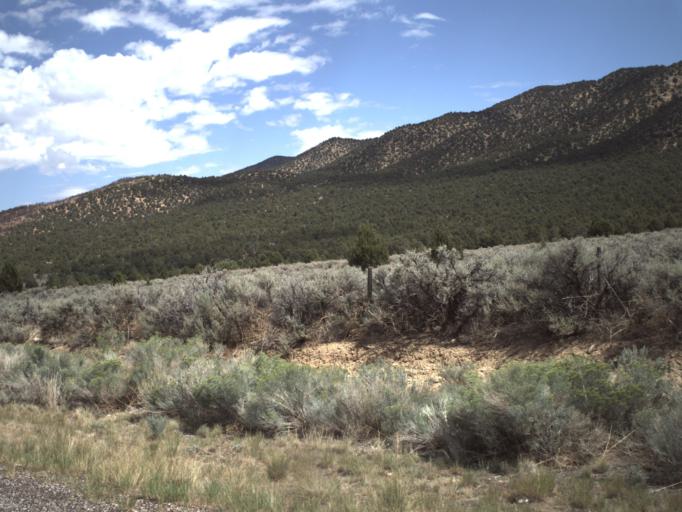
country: US
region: Utah
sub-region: Sanpete County
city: Gunnison
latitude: 39.1689
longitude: -112.0746
